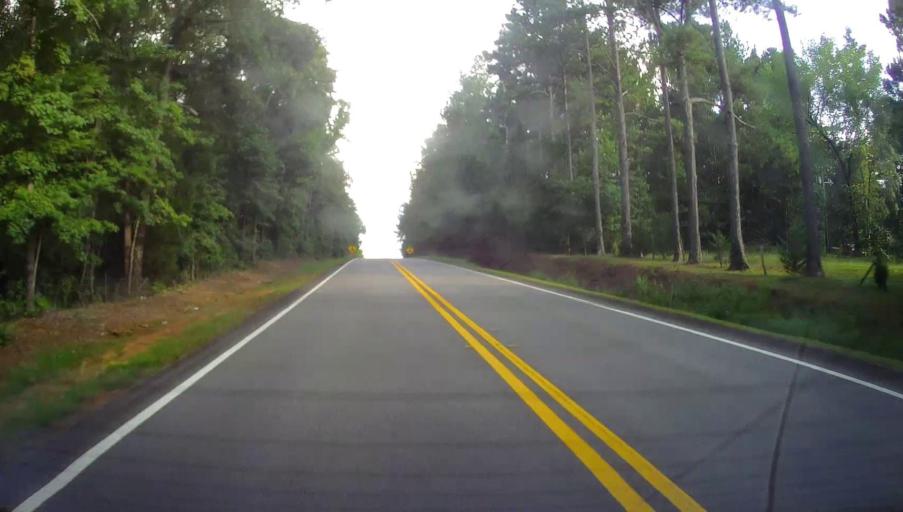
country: US
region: Georgia
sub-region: Crawford County
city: Knoxville
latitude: 32.8810
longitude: -83.9960
